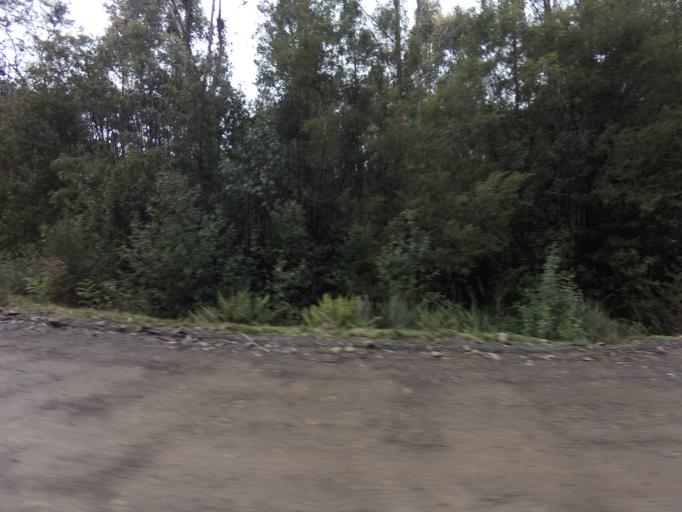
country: AU
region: Tasmania
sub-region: Huon Valley
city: Geeveston
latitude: -43.4769
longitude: 146.8916
